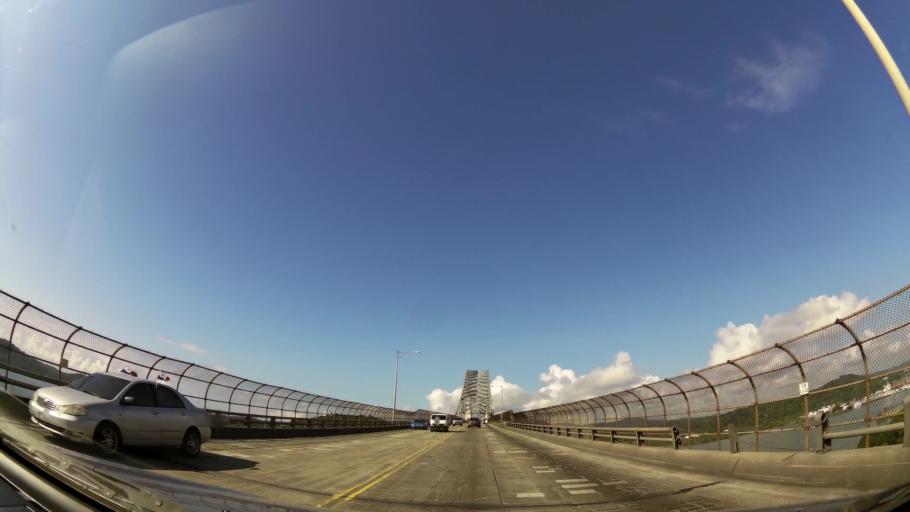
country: PA
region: Panama
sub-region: Distrito de Panama
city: Ancon
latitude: 8.9449
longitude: -79.5614
